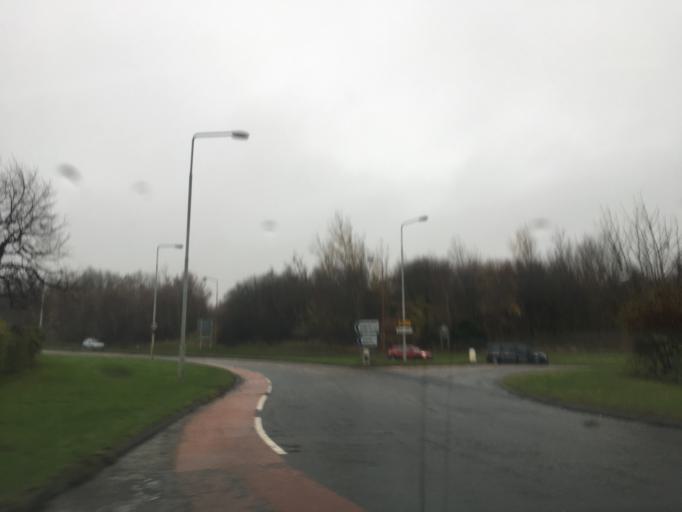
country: GB
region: Scotland
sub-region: Edinburgh
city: Colinton
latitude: 55.9108
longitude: -3.2784
